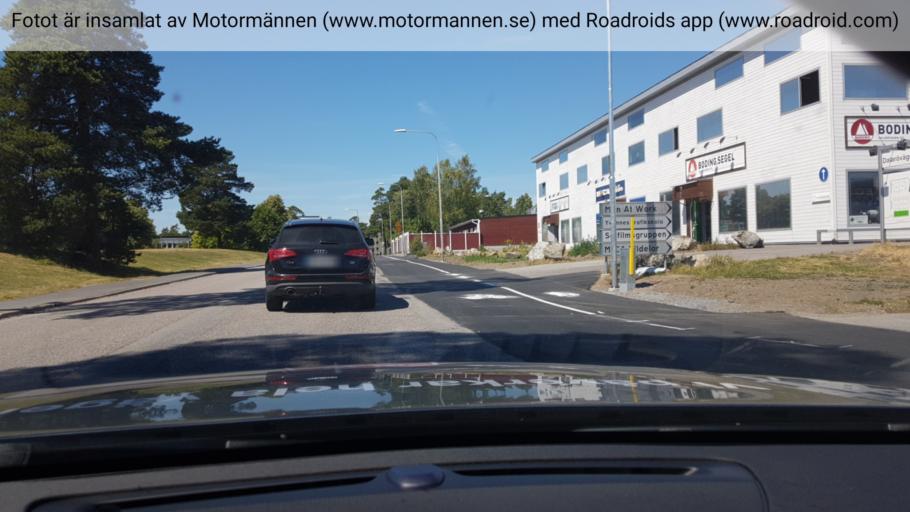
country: SE
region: Stockholm
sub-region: Haninge Kommun
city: Haninge
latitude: 59.1675
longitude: 18.1540
